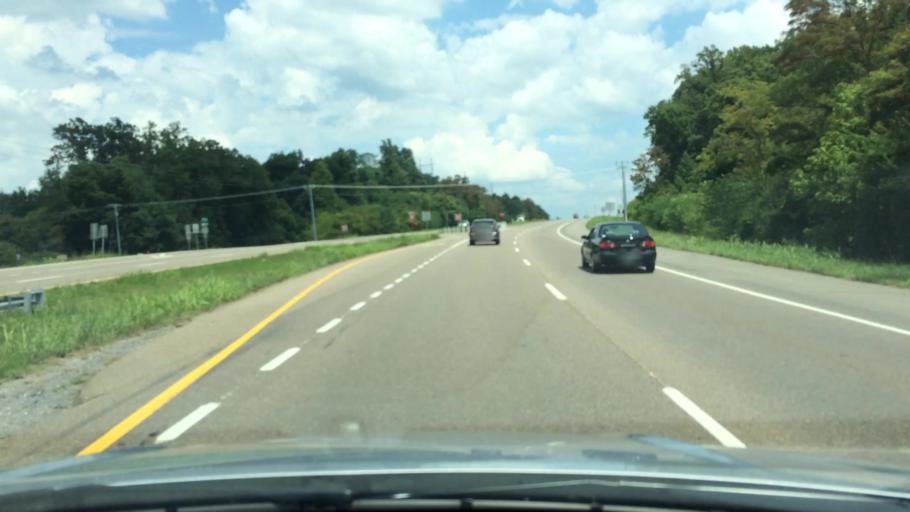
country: US
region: Tennessee
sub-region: Hamblen County
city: Morristown
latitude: 36.1880
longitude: -83.3058
